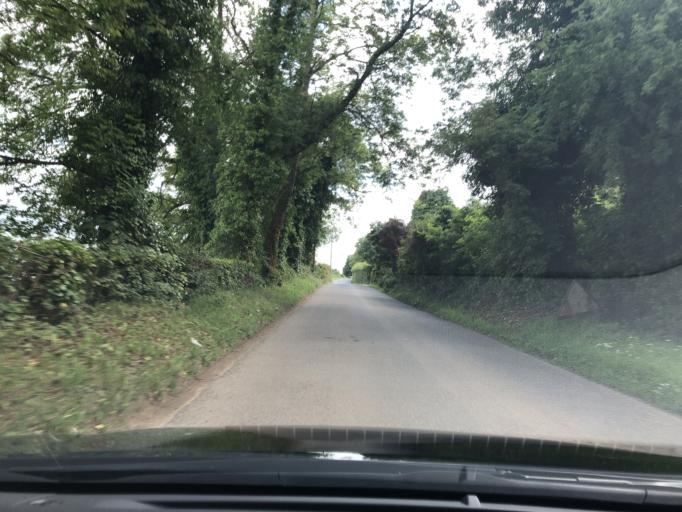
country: GB
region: Northern Ireland
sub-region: Ards District
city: Newtownards
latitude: 54.5790
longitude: -5.7108
